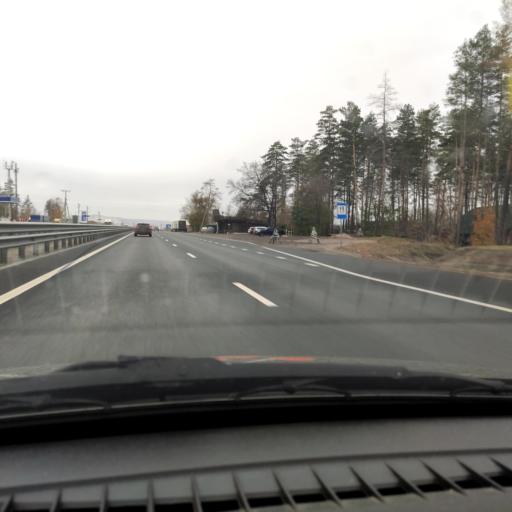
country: RU
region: Samara
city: Zhigulevsk
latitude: 53.5048
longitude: 49.5520
